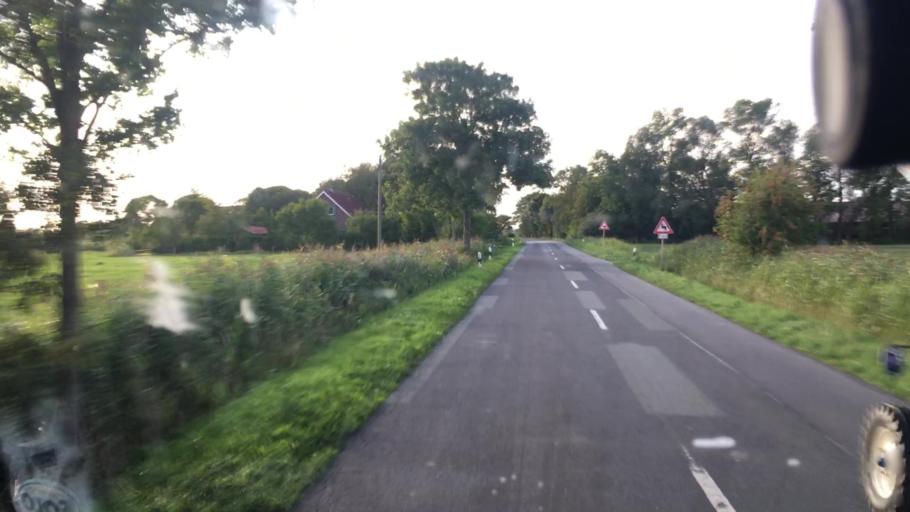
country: DE
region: Lower Saxony
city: Werdum
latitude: 53.6672
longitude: 7.7299
